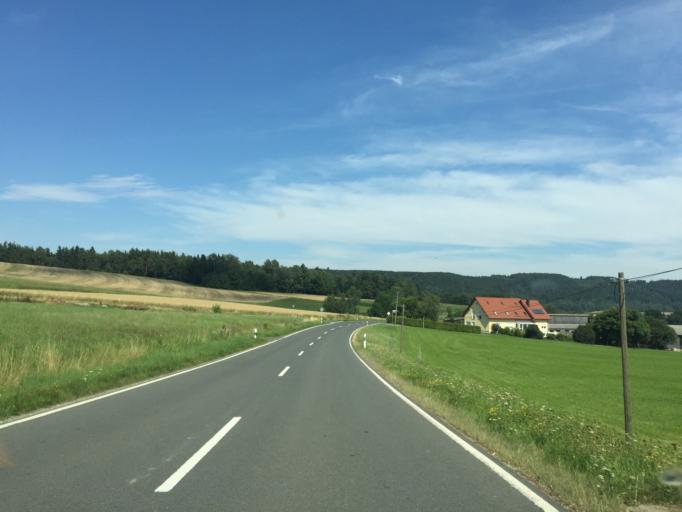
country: DE
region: Bavaria
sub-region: Upper Palatinate
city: Parkstein
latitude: 49.7802
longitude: 12.0381
